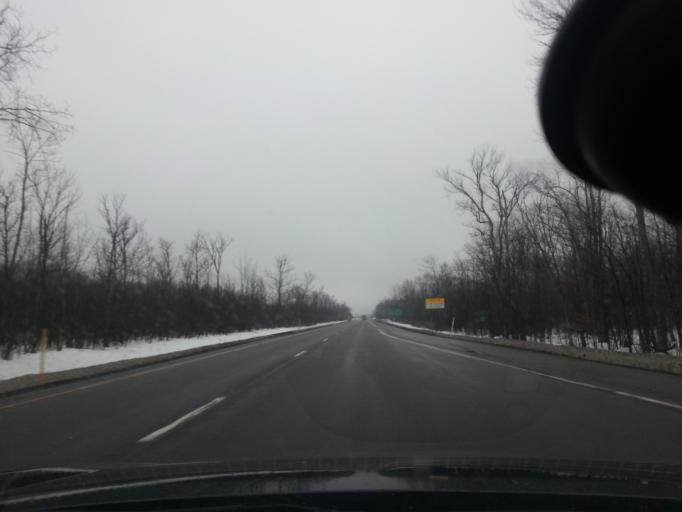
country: US
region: New York
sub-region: Jefferson County
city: Adams
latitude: 43.7197
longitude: -76.0769
